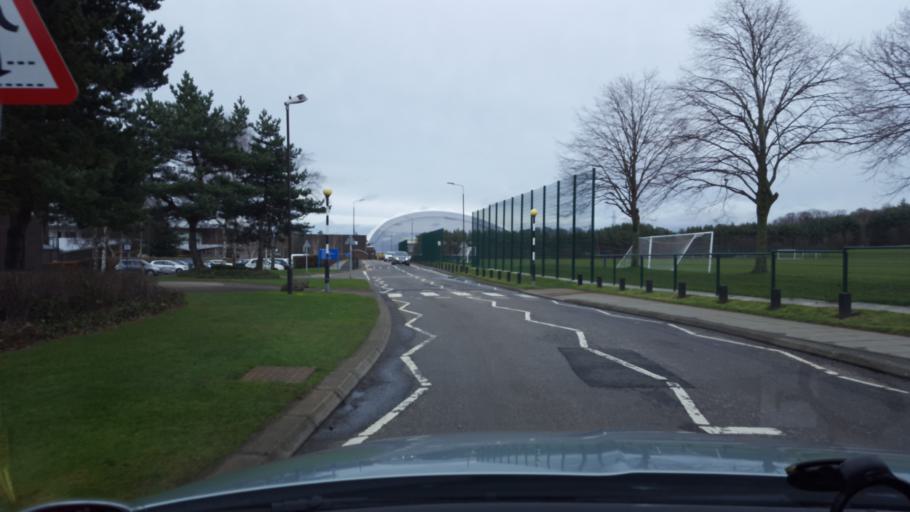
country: GB
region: Scotland
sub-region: Edinburgh
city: Currie
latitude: 55.9071
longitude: -3.3219
